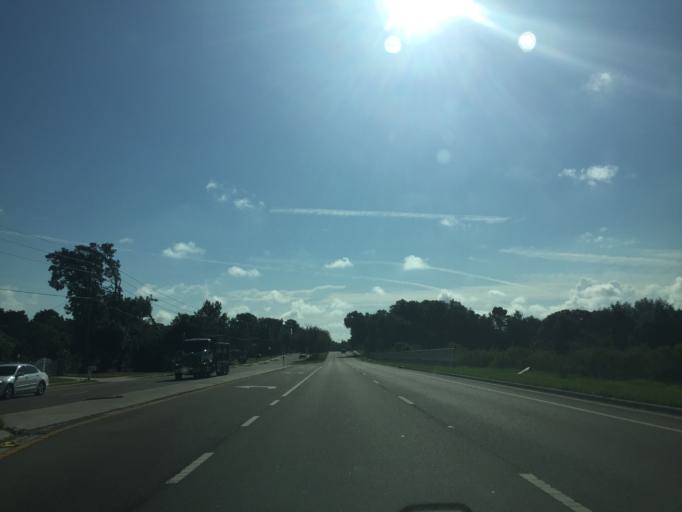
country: US
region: Florida
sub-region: Seminole County
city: Winter Springs
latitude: 28.6705
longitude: -81.2964
